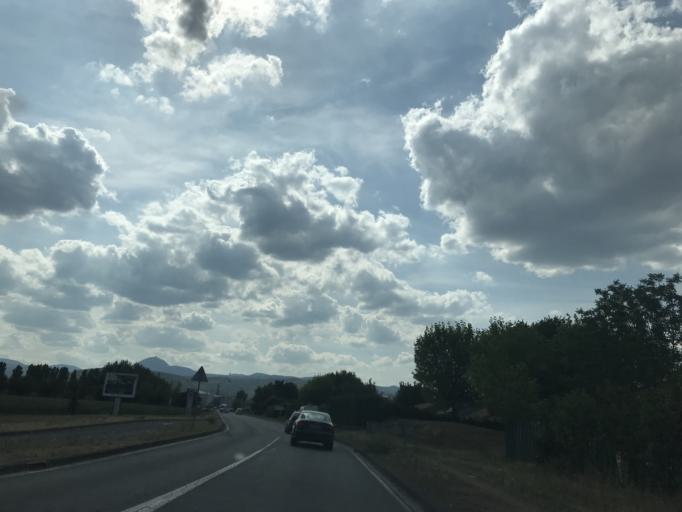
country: FR
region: Auvergne
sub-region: Departement du Puy-de-Dome
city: Gerzat
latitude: 45.8145
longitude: 3.1433
